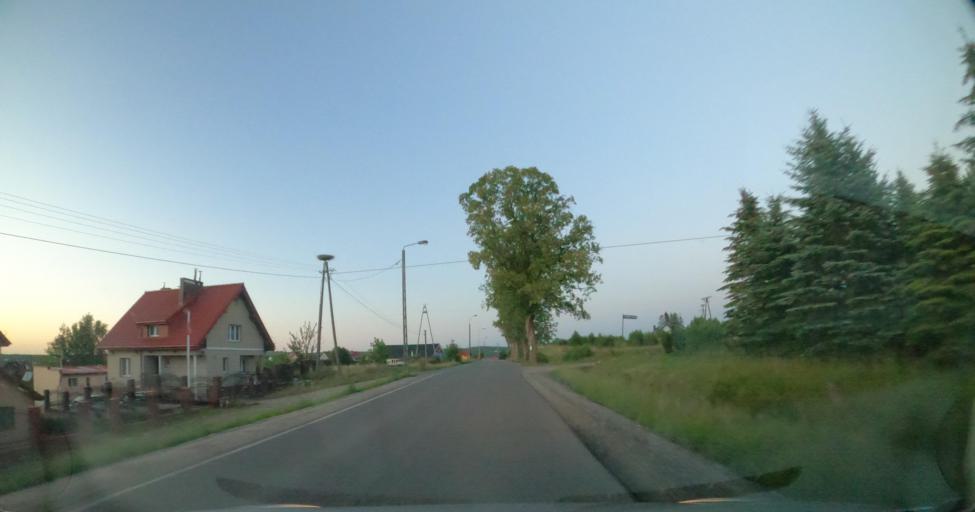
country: PL
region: Pomeranian Voivodeship
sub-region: Powiat wejherowski
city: Szemud
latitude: 54.4836
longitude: 18.2126
